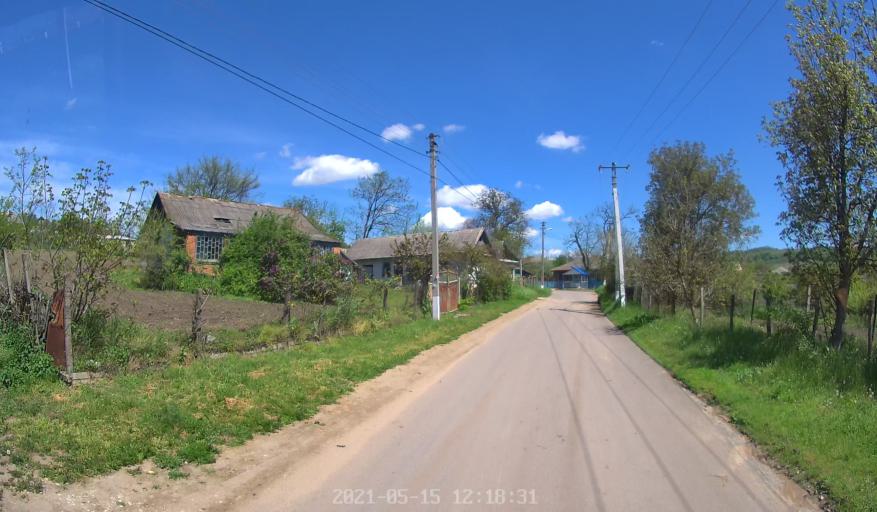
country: MD
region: Hincesti
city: Hincesti
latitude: 46.7978
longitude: 28.5412
